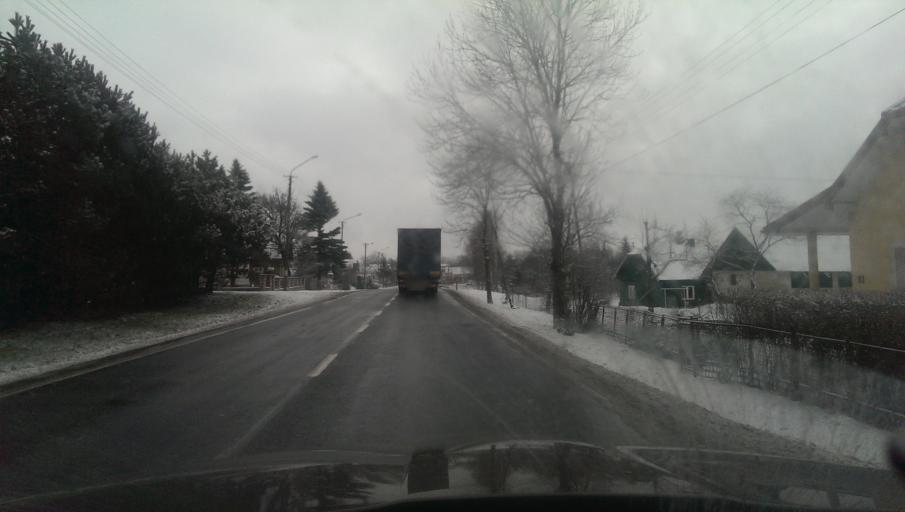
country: PL
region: Subcarpathian Voivodeship
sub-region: Powiat sanocki
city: Nowosielce-Gniewosz
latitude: 49.5608
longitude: 22.0899
